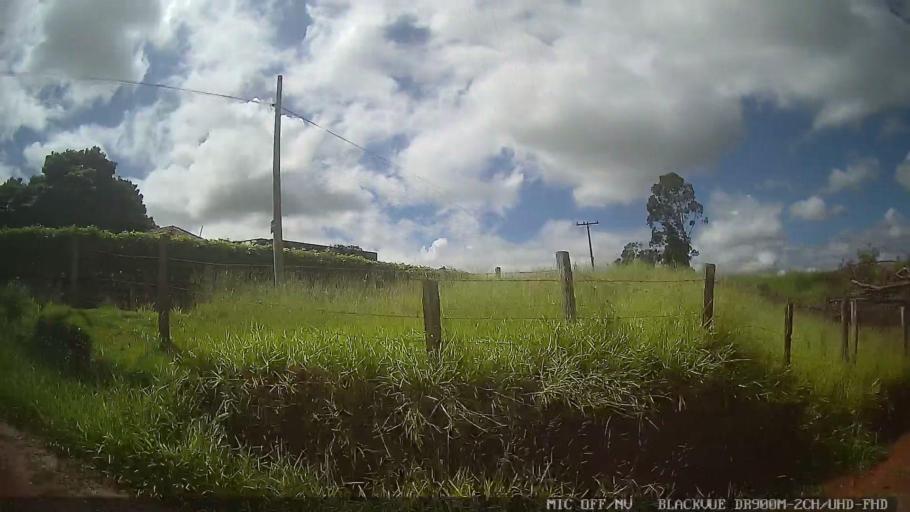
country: BR
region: Sao Paulo
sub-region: Amparo
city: Amparo
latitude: -22.8609
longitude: -46.7173
